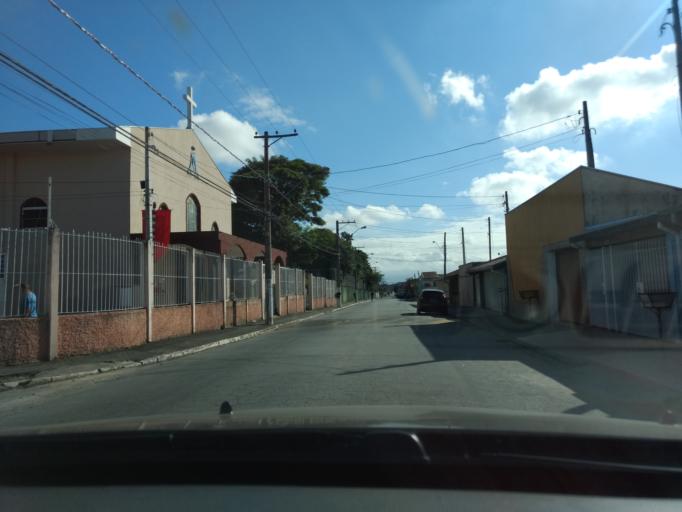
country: BR
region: Sao Paulo
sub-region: Taubate
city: Taubate
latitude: -22.9998
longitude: -45.5287
